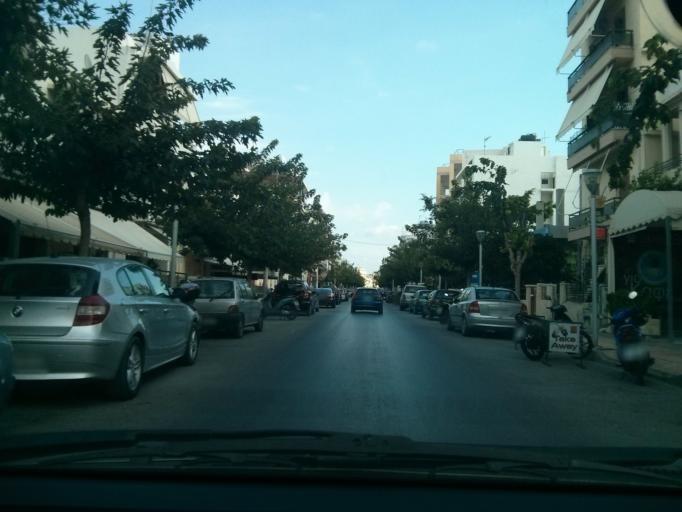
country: GR
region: Crete
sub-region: Nomos Irakleiou
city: Irakleion
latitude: 35.3308
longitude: 25.1359
